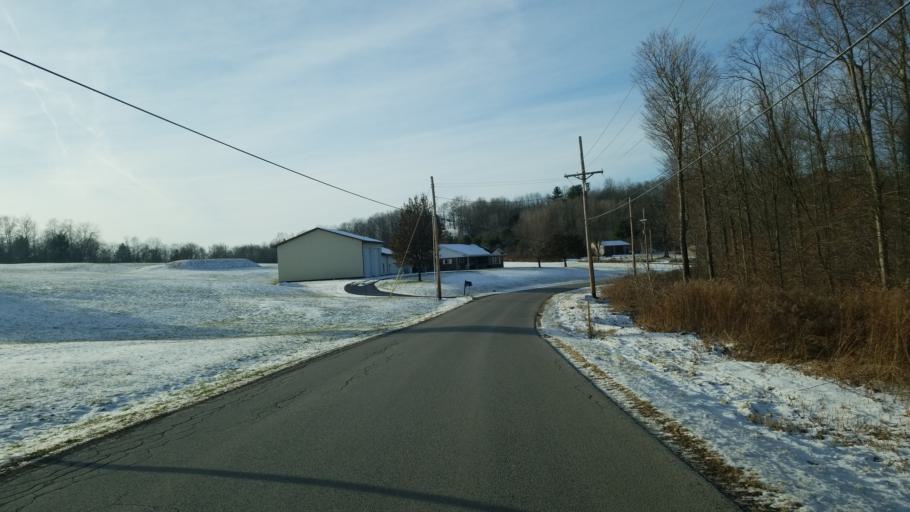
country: US
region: Pennsylvania
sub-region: Clearfield County
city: DuBois
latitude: 41.1123
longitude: -78.7035
